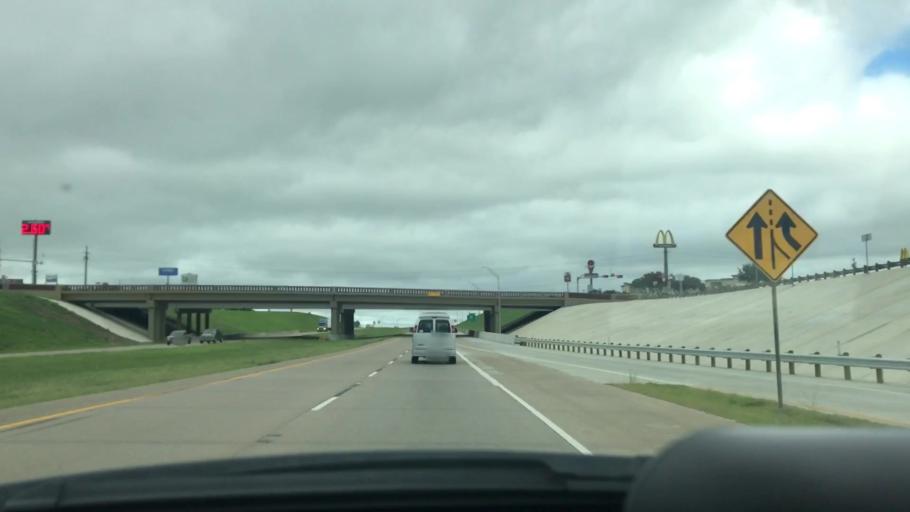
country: US
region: Texas
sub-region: Grayson County
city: Denison
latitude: 33.7607
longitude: -96.5851
